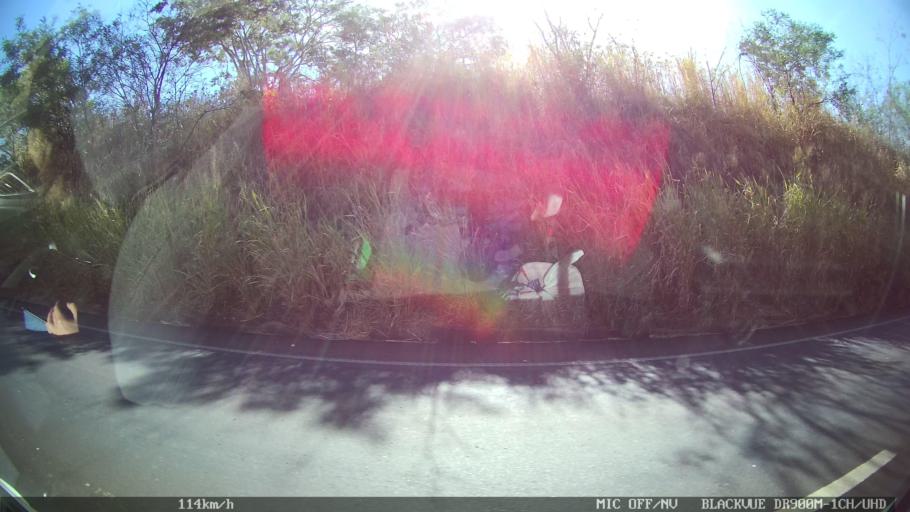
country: BR
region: Sao Paulo
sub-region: Olimpia
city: Olimpia
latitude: -20.6196
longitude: -48.7657
